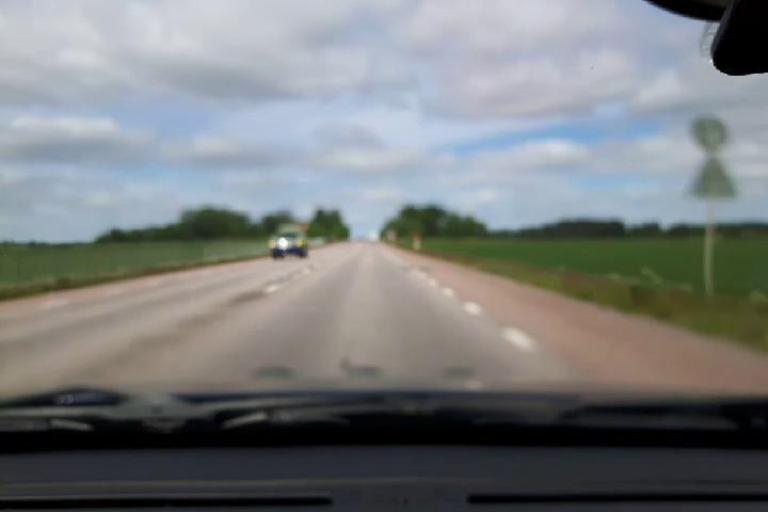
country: SE
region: Uppsala
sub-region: Uppsala Kommun
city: Gamla Uppsala
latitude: 59.9021
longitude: 17.6116
